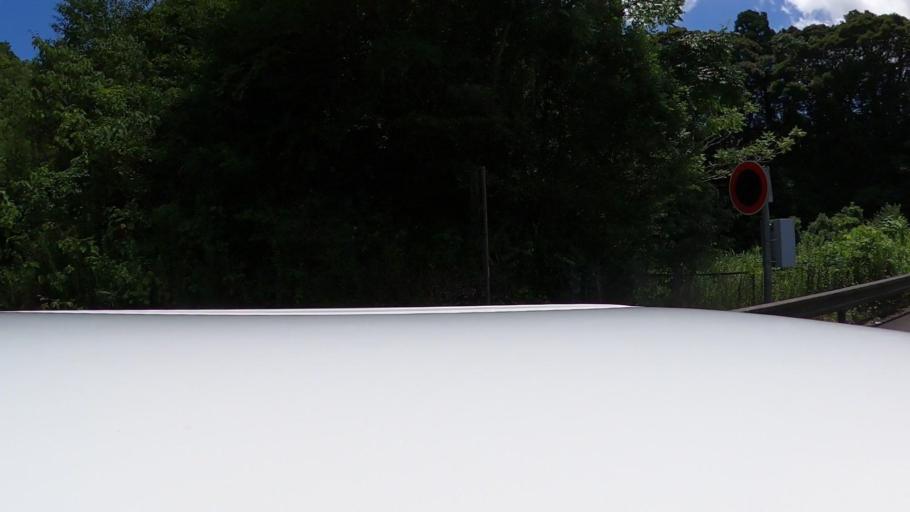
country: JP
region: Miyazaki
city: Nobeoka
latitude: 32.5720
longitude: 131.5652
